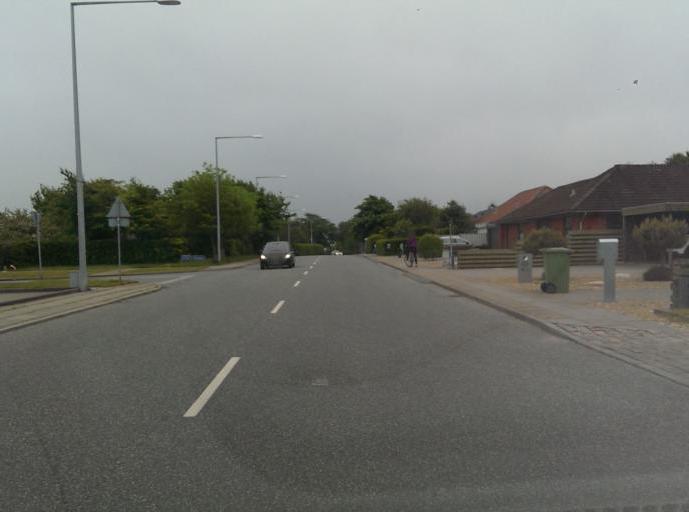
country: DK
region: South Denmark
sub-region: Fano Kommune
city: Nordby
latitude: 55.5169
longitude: 8.3715
